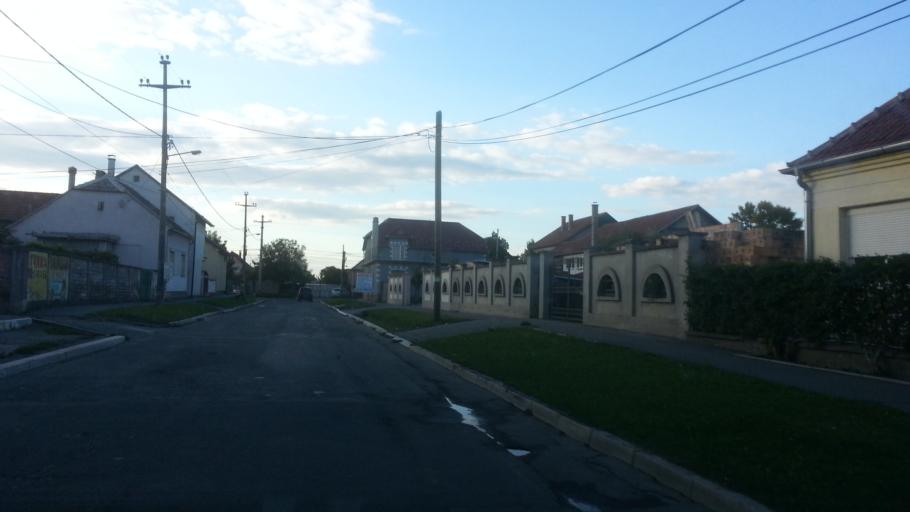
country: RS
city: Novi Banovci
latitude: 44.9013
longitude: 20.2756
